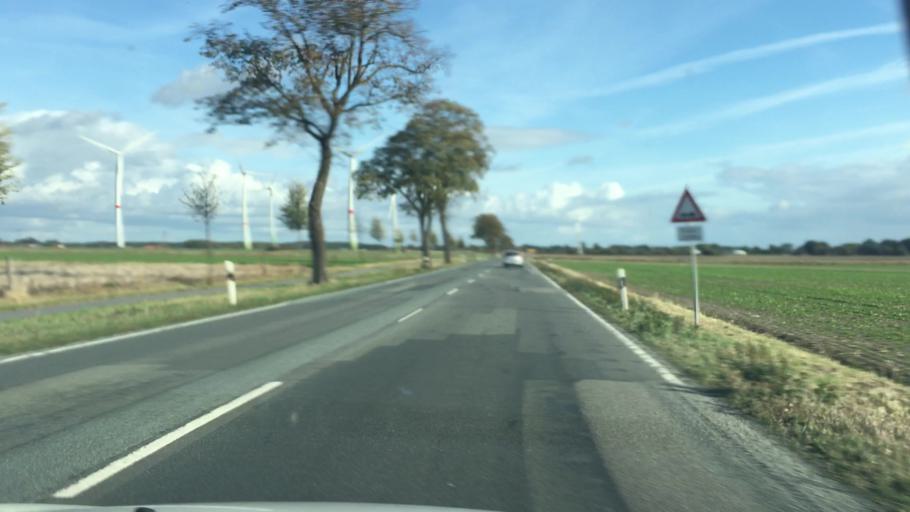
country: DE
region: Lower Saxony
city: Siedenburg
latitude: 52.6732
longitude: 8.9328
